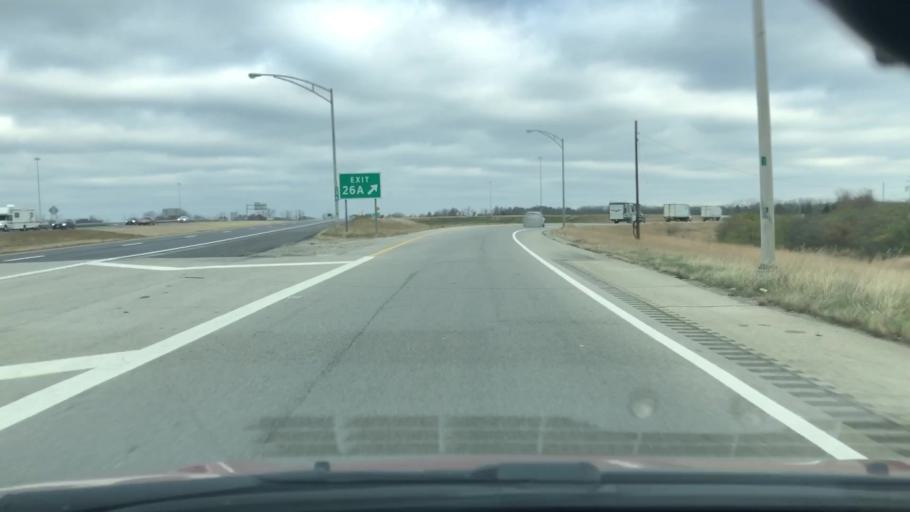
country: US
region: Ohio
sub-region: Clark County
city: Holiday Valley
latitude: 39.8610
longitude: -83.9936
